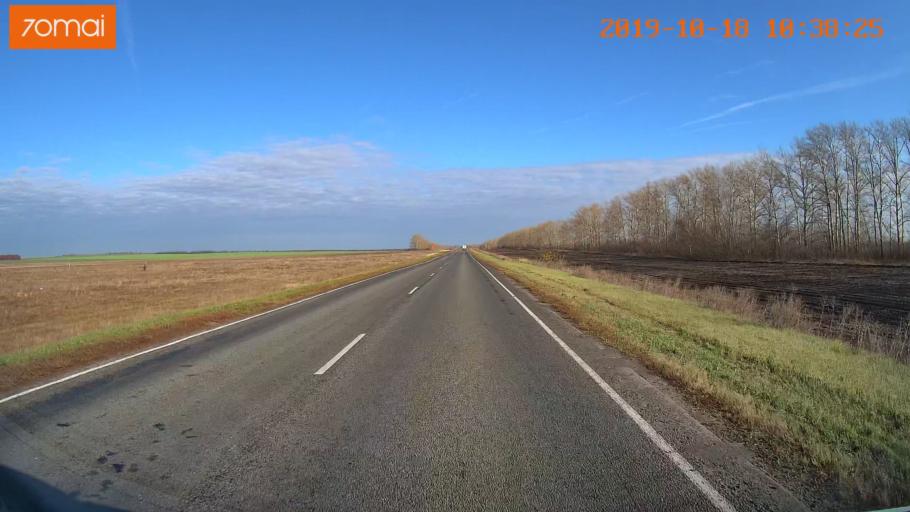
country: RU
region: Tula
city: Kurkino
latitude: 53.5727
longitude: 38.6413
